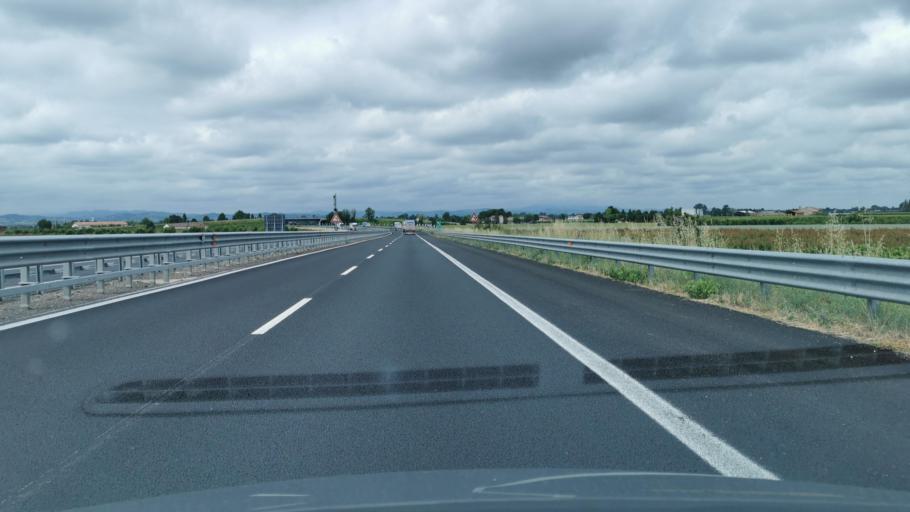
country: IT
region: Emilia-Romagna
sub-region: Provincia di Ravenna
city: Solarolo
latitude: 44.3682
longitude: 11.8377
